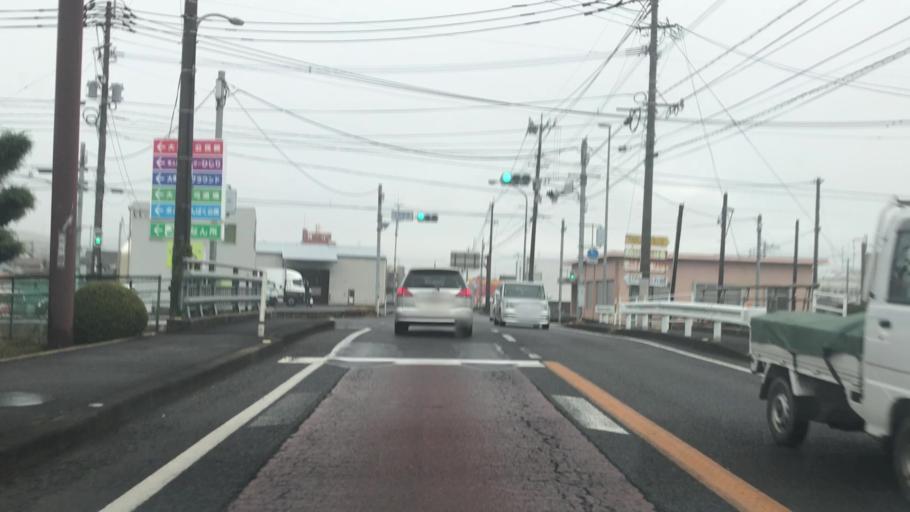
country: JP
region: Saga Prefecture
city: Takeocho-takeo
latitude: 33.2128
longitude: 130.1098
